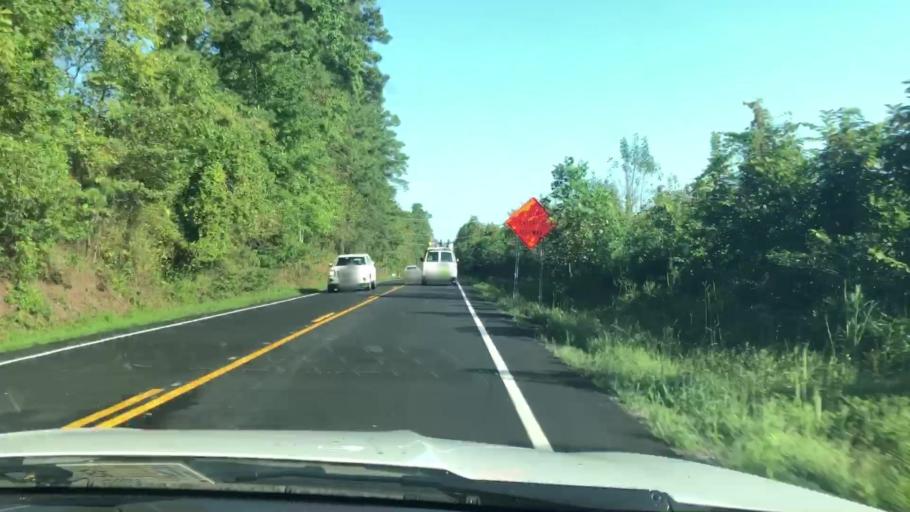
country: US
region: Virginia
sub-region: King William County
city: West Point
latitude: 37.4738
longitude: -76.8456
